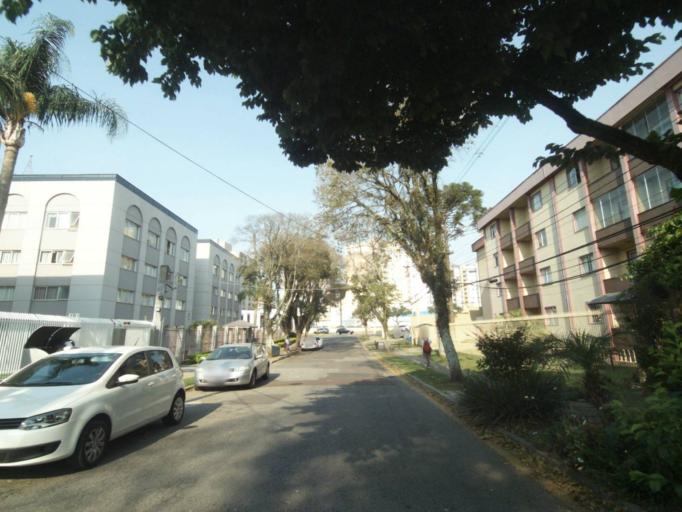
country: BR
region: Parana
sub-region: Curitiba
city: Curitiba
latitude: -25.4672
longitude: -49.2961
